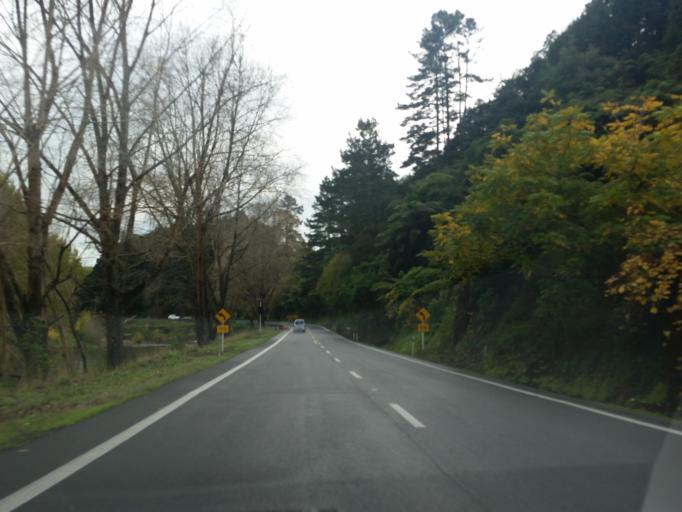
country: NZ
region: Waikato
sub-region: Hauraki District
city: Paeroa
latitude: -37.4149
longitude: 175.7158
